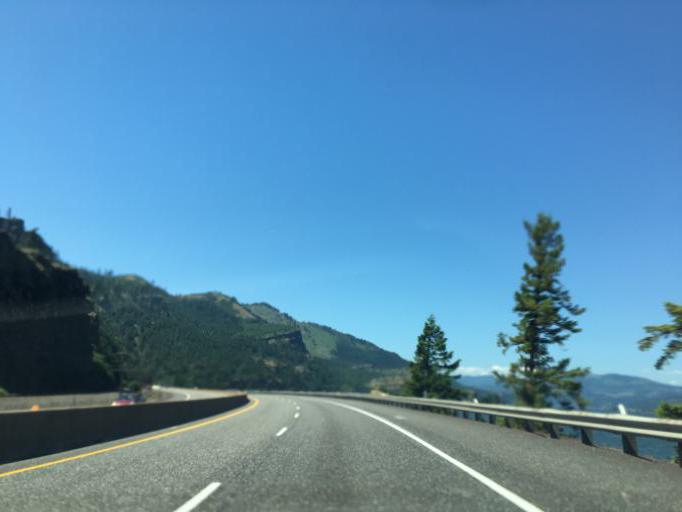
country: US
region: Washington
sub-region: Klickitat County
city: White Salmon
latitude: 45.6877
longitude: -121.4111
